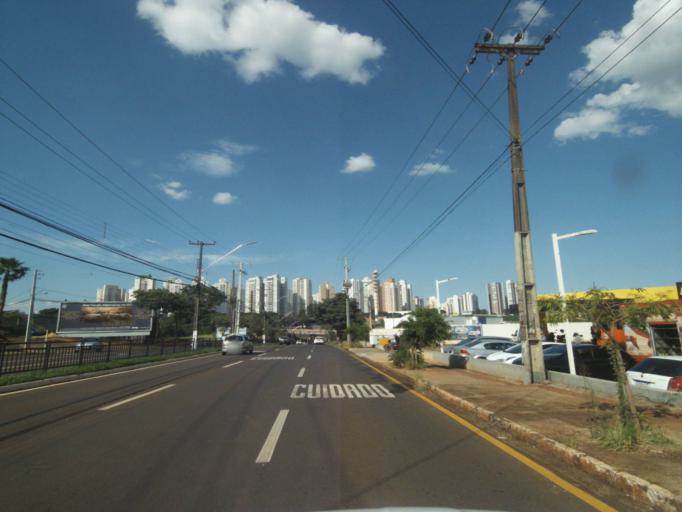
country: BR
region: Parana
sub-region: Londrina
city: Londrina
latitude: -23.3388
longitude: -51.1858
